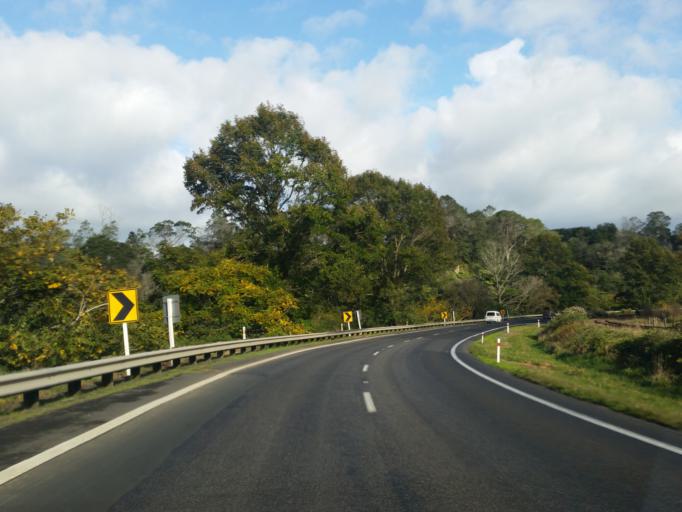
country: NZ
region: Waikato
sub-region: Hauraki District
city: Waihi
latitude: -37.4175
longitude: 175.7871
